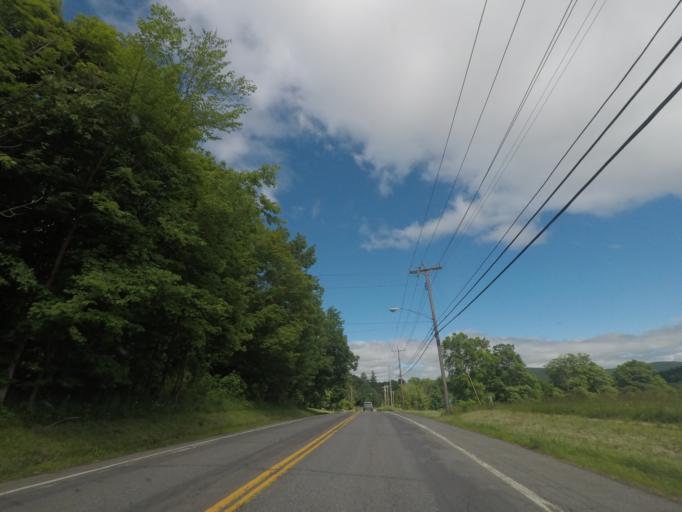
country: US
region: New York
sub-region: Columbia County
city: Philmont
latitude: 42.1817
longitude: -73.5357
